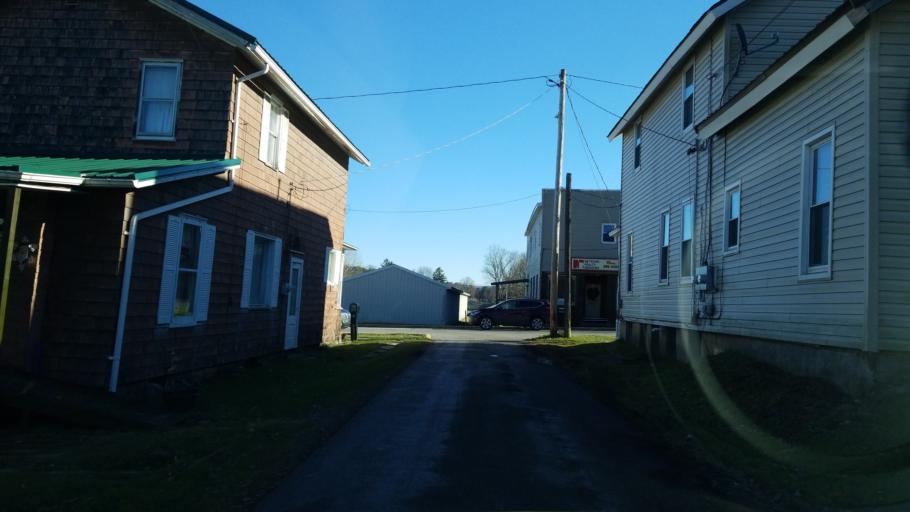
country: US
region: Pennsylvania
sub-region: Jefferson County
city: Brockway
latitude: 41.2482
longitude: -78.7989
